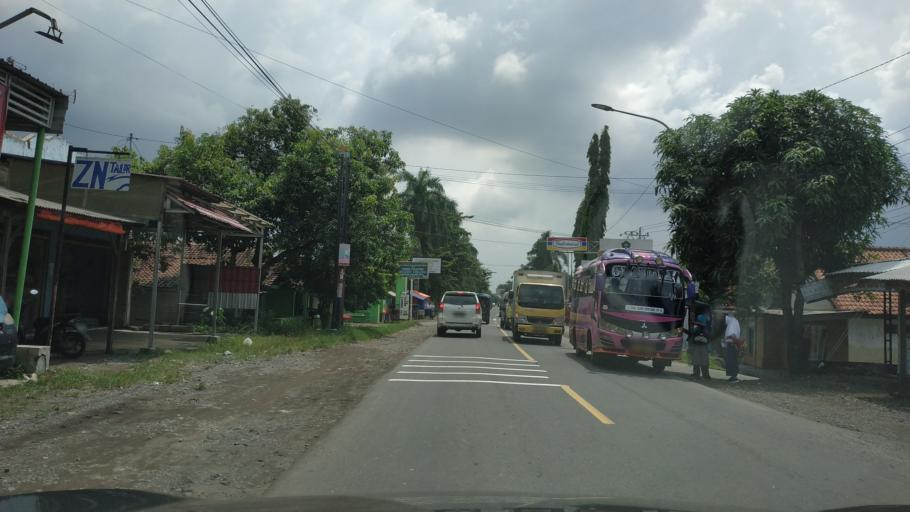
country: ID
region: Central Java
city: Lebaksiu
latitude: -7.0211
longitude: 109.1420
